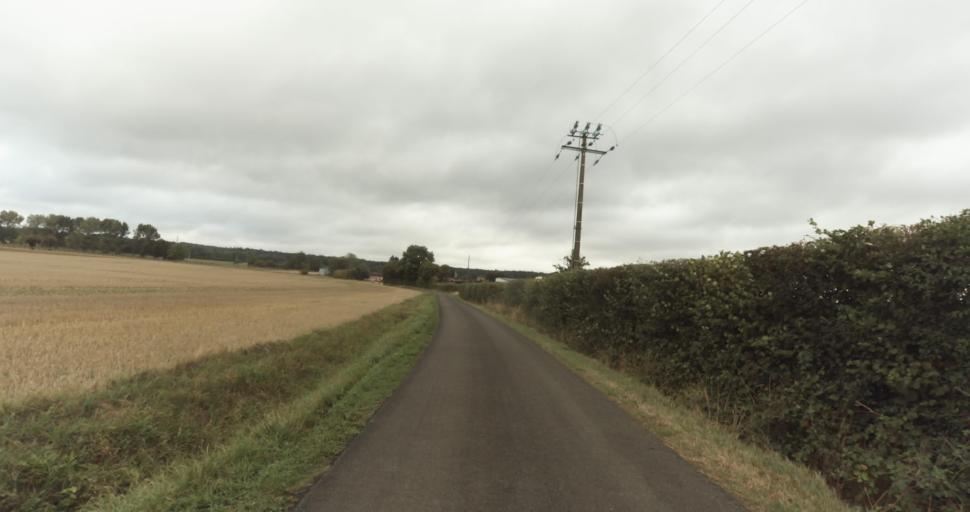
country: FR
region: Lower Normandy
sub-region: Departement de l'Orne
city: Sainte-Gauburge-Sainte-Colombe
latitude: 48.7382
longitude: 0.4703
